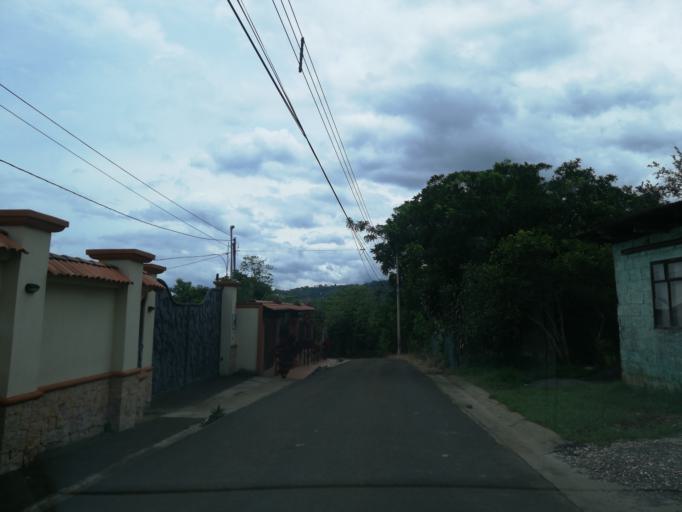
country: CR
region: Heredia
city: Santo Domingo
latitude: 10.0429
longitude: -84.1839
